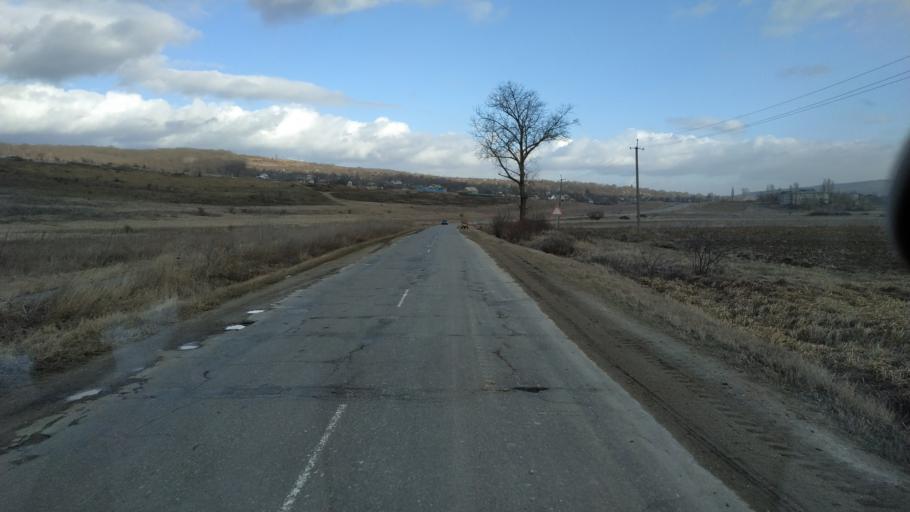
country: MD
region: Calarasi
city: Calarasi
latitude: 47.3276
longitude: 28.0976
